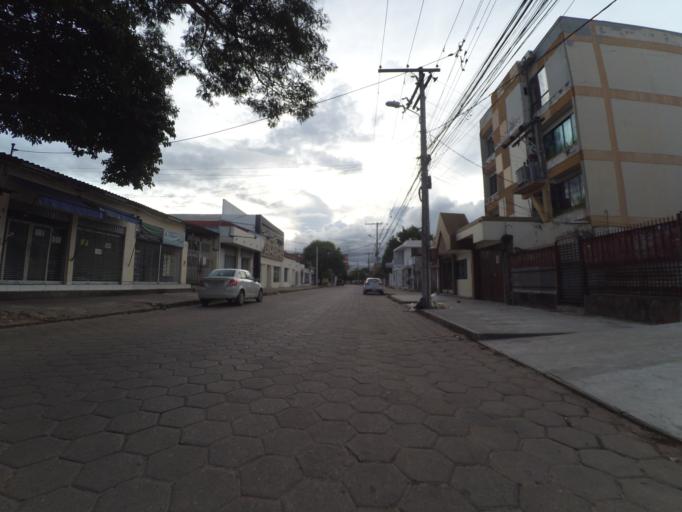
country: BO
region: Santa Cruz
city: Santa Cruz de la Sierra
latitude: -17.7880
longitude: -63.1893
